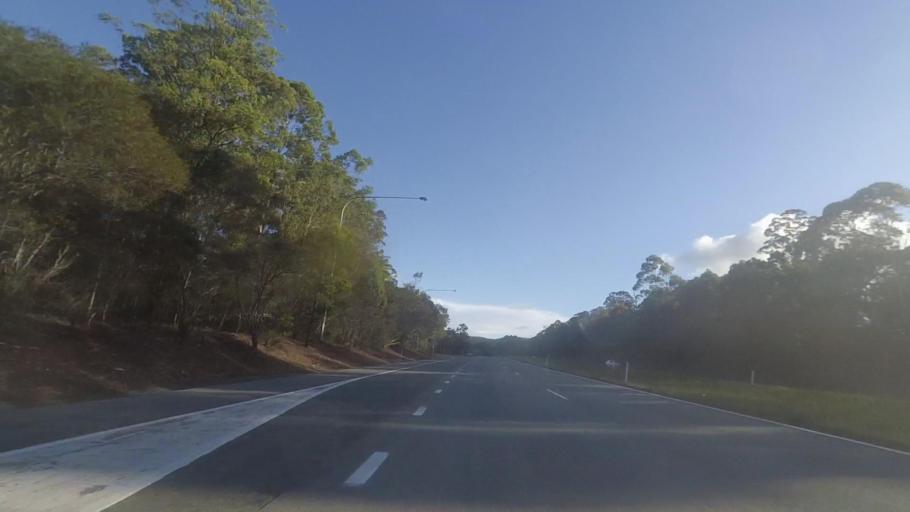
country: AU
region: New South Wales
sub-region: Great Lakes
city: Nabiac
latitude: -32.2497
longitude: 152.3231
